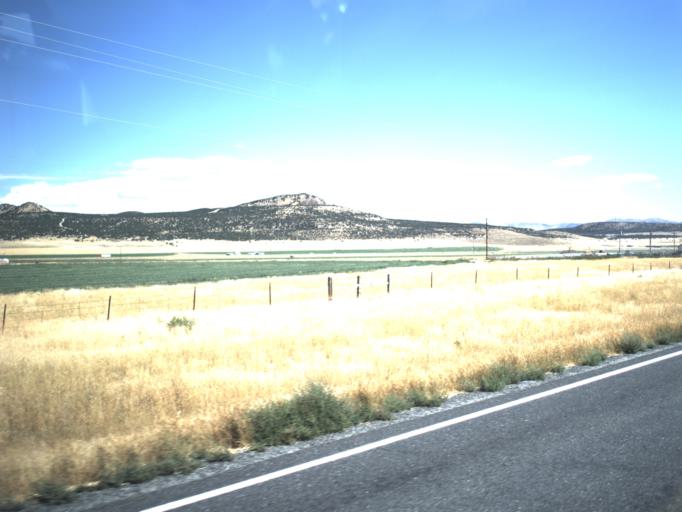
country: US
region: Idaho
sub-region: Oneida County
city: Malad City
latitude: 41.9674
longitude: -112.8093
